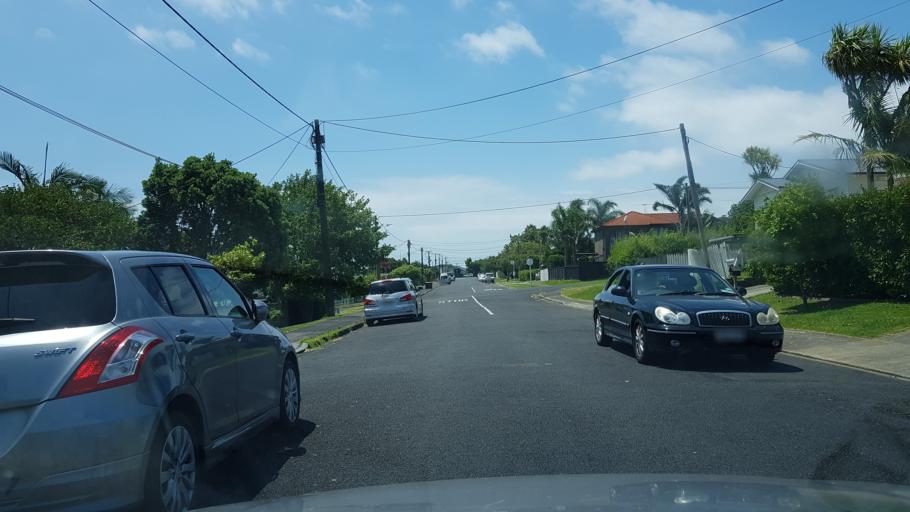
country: NZ
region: Auckland
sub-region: Auckland
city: North Shore
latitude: -36.8146
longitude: 174.7893
